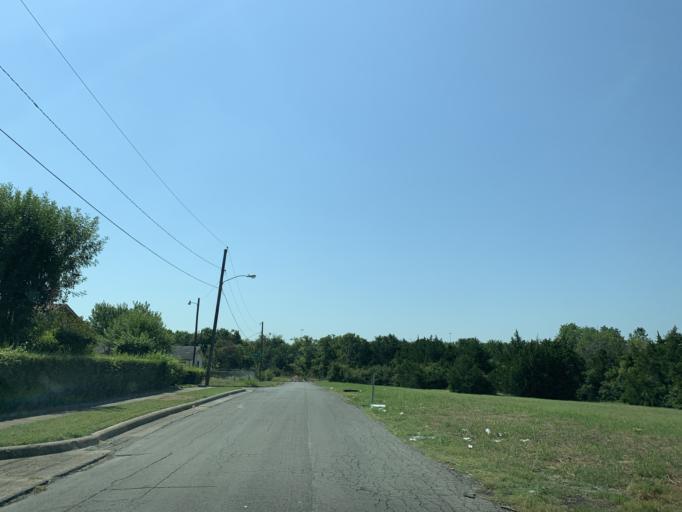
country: US
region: Texas
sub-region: Dallas County
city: Hutchins
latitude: 32.6596
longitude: -96.7590
